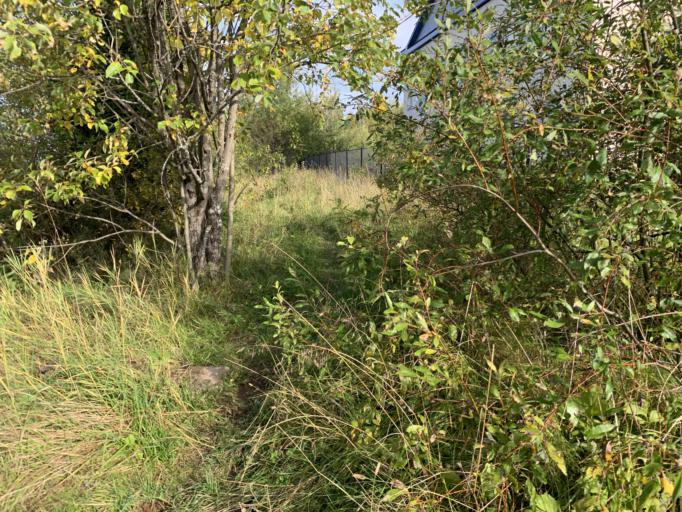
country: RU
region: Perm
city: Gubakha
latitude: 58.8348
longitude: 57.5603
